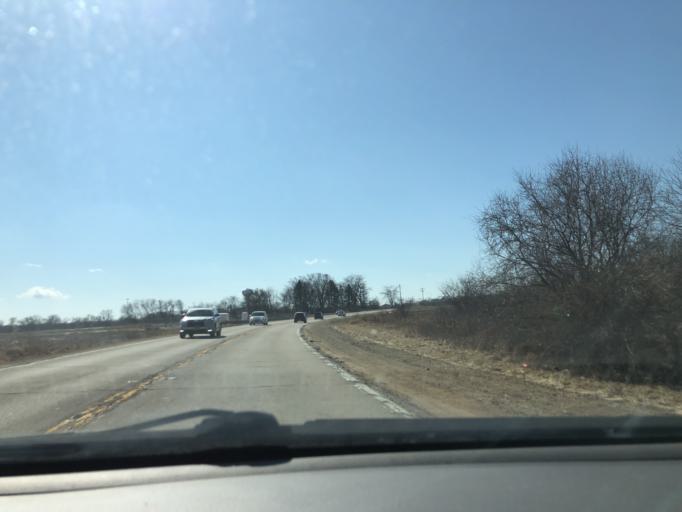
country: US
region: Illinois
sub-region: Kane County
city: Pingree Grove
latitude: 42.0957
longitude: -88.4546
